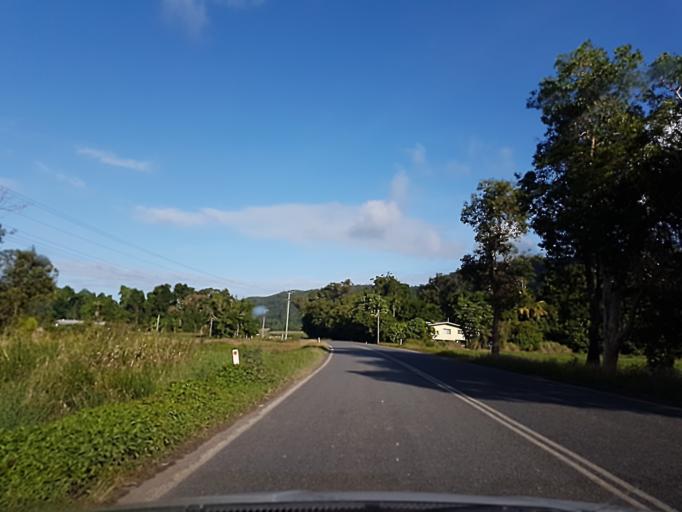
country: AU
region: Queensland
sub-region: Cairns
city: Port Douglas
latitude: -16.3044
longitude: 145.3900
